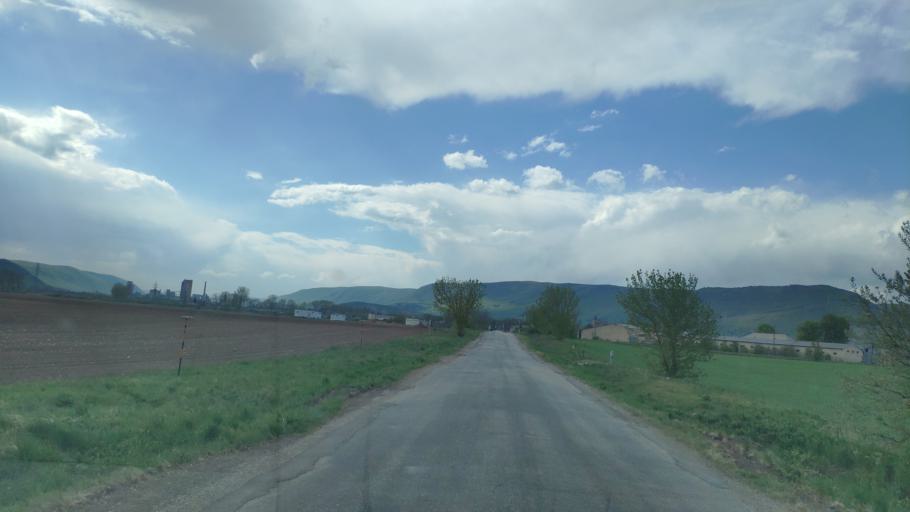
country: SK
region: Kosicky
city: Medzev
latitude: 48.5948
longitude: 20.8898
